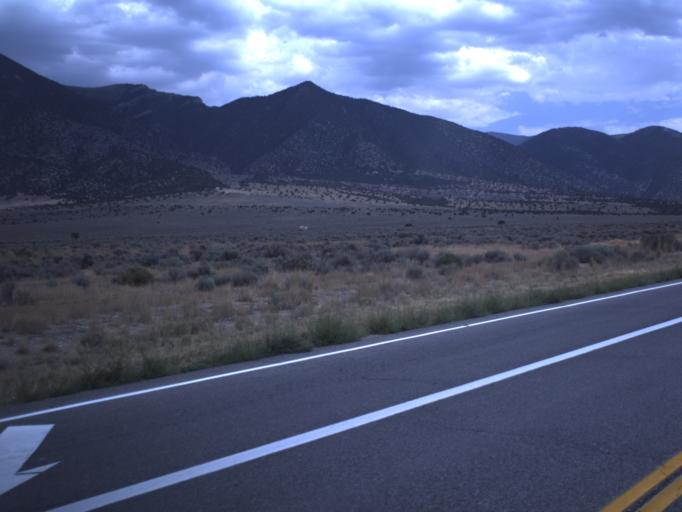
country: US
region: Utah
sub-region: Tooele County
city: Tooele
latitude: 40.3623
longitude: -112.3331
